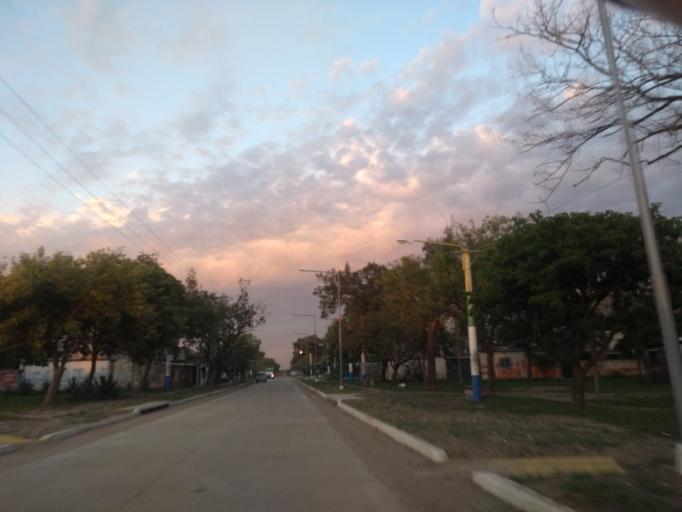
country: AR
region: Chaco
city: Resistencia
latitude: -27.4833
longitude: -58.9863
